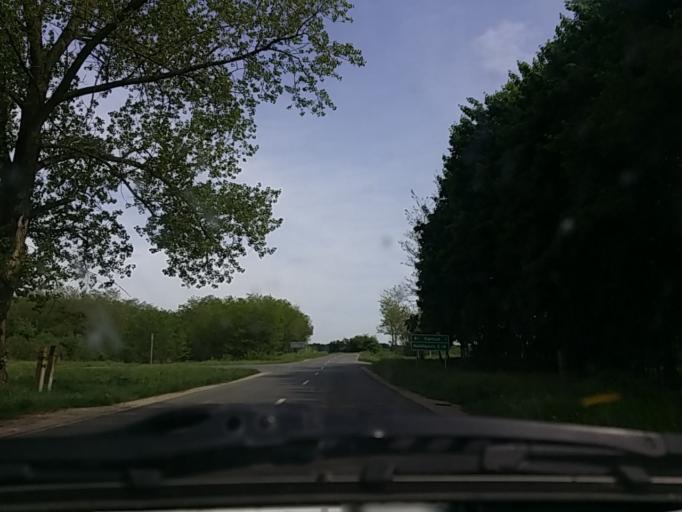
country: HU
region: Baranya
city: Vajszlo
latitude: 45.8442
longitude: 18.0401
